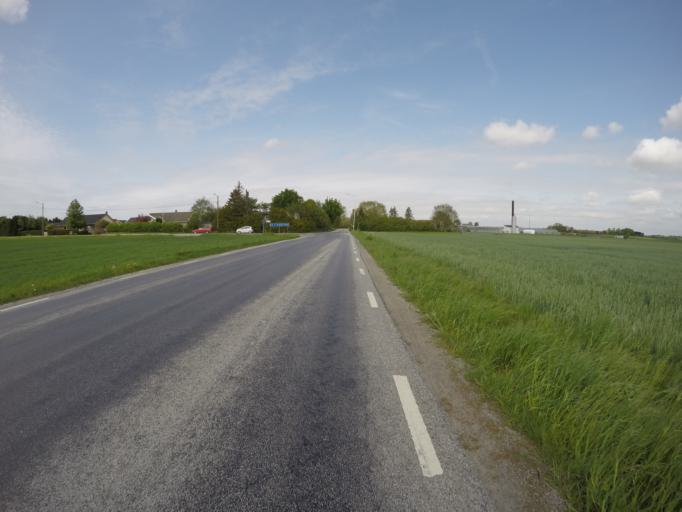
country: SE
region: Skane
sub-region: Malmo
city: Tygelsjo
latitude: 55.5289
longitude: 13.0252
